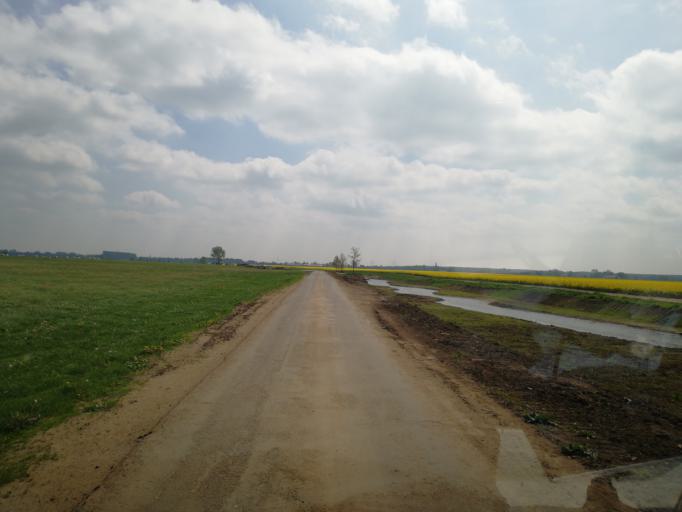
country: DE
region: Brandenburg
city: Doberlug-Kirchhain
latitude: 51.6715
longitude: 13.5374
